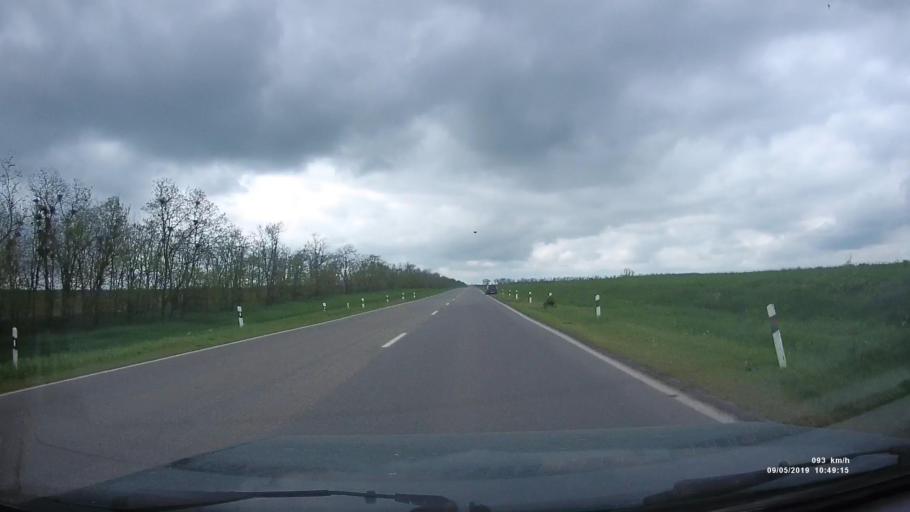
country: RU
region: Rostov
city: Peshkovo
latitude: 46.9450
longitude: 39.3555
